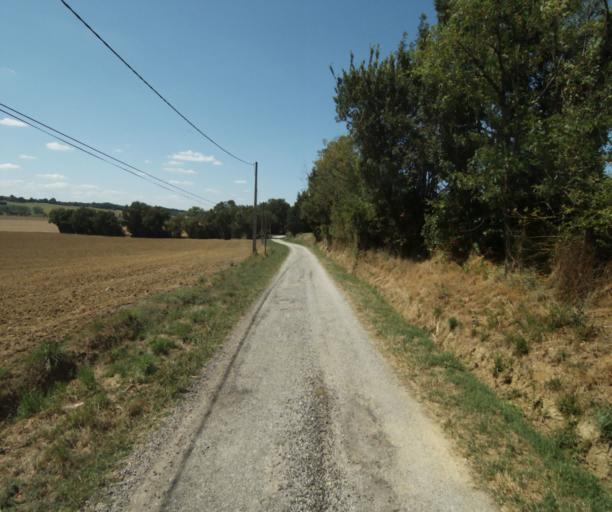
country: FR
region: Midi-Pyrenees
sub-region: Departement de la Haute-Garonne
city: Saint-Felix-Lauragais
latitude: 43.4916
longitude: 1.8850
